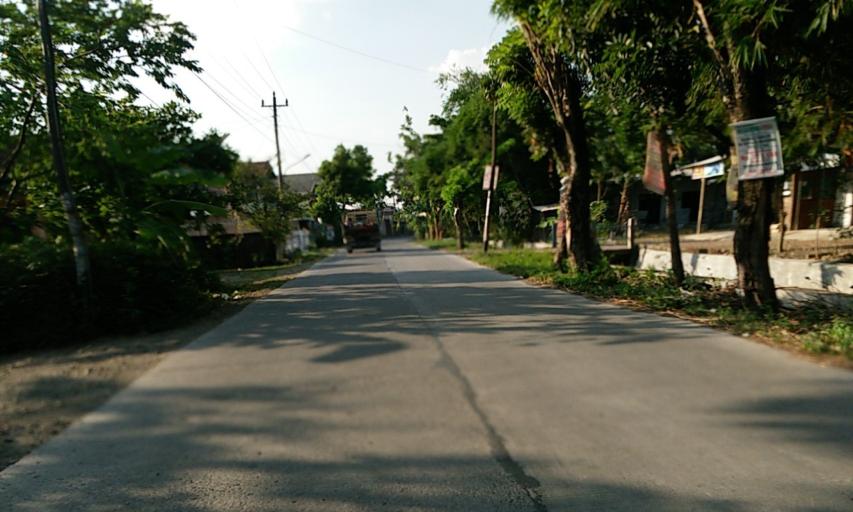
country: ID
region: Central Java
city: Mranggen
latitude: -7.0117
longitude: 110.4874
